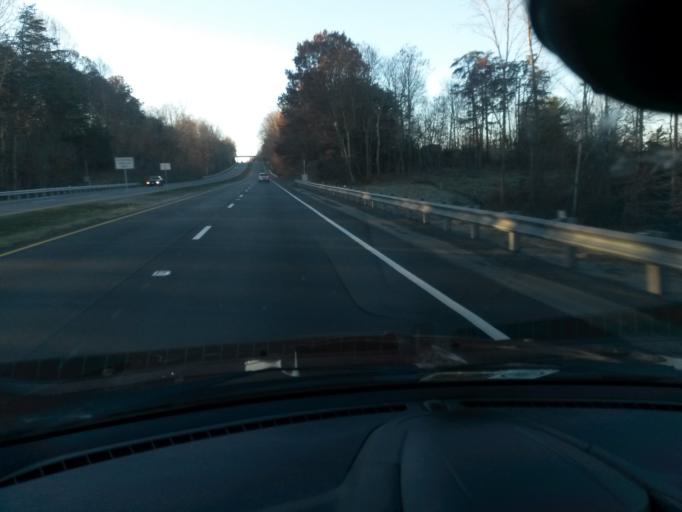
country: US
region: Virginia
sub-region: Franklin County
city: Henry Fork
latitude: 36.9884
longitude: -79.8706
